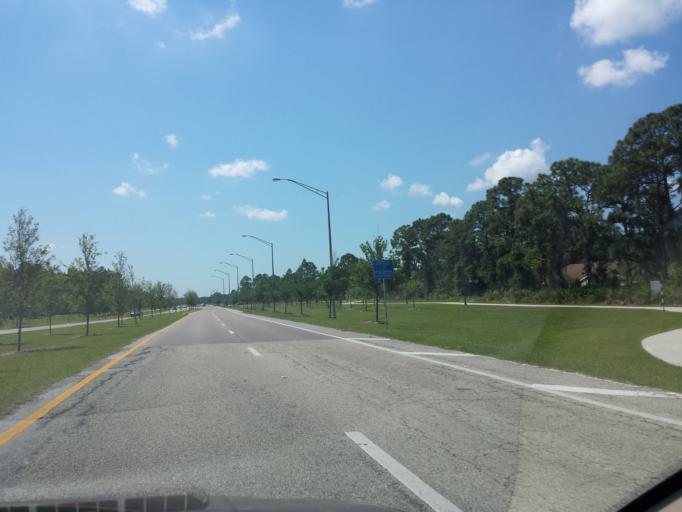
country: US
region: Florida
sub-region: Sarasota County
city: North Port
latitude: 27.0845
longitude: -82.2089
